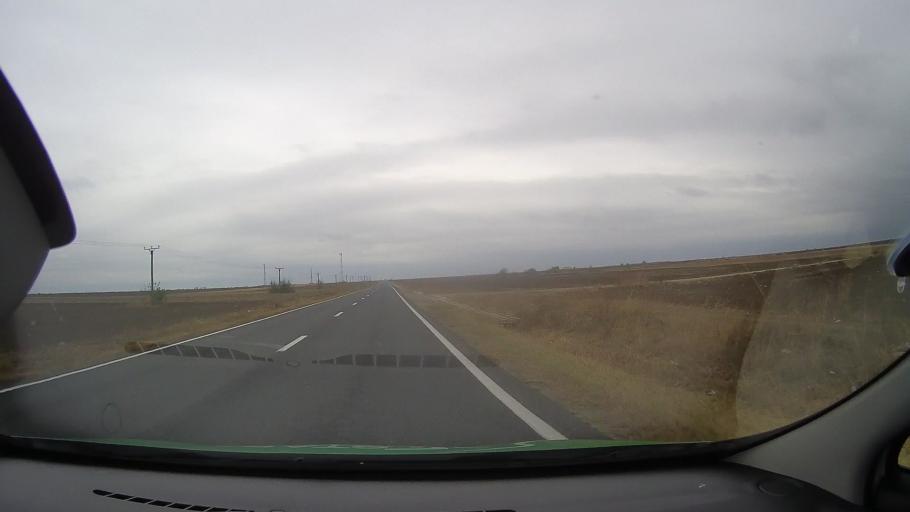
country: RO
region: Constanta
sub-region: Comuna Nicolae Balcescu
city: Nicolae Balcescu
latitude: 44.3767
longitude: 28.4193
